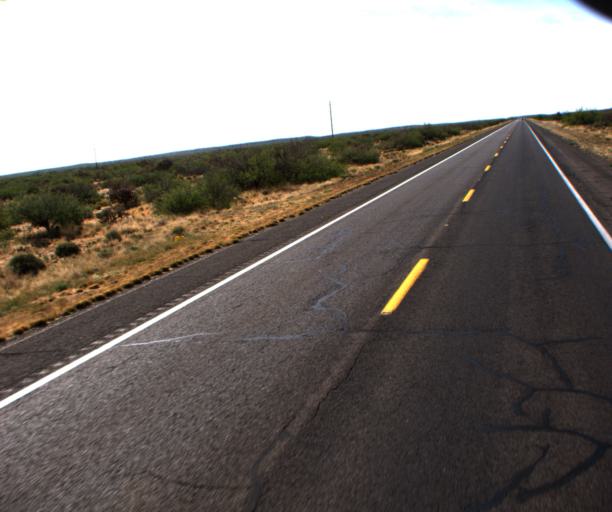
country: US
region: Arizona
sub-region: Graham County
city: Swift Trail Junction
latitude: 32.6744
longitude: -109.7045
